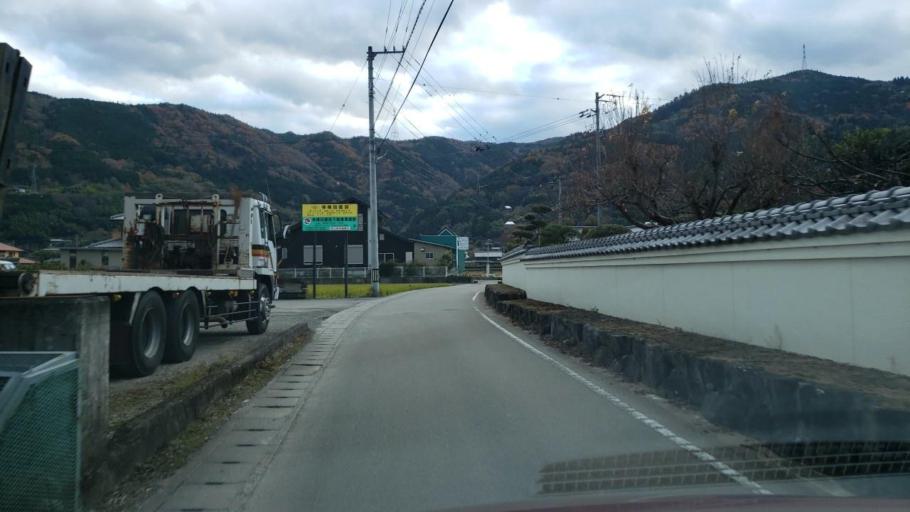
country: JP
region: Tokushima
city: Wakimachi
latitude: 34.0599
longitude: 134.1434
